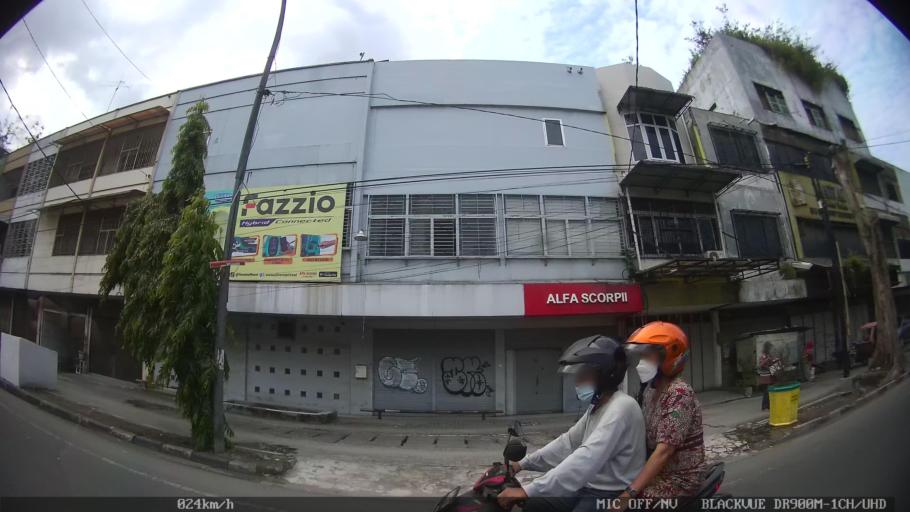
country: ID
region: North Sumatra
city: Medan
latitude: 3.5945
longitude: 98.6807
